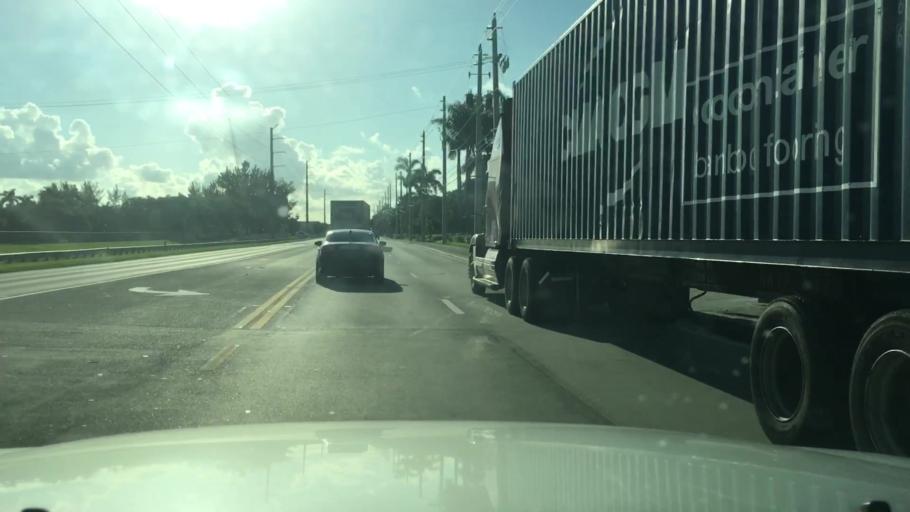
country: US
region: Florida
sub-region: Miami-Dade County
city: Sweetwater
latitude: 25.7966
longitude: -80.3831
